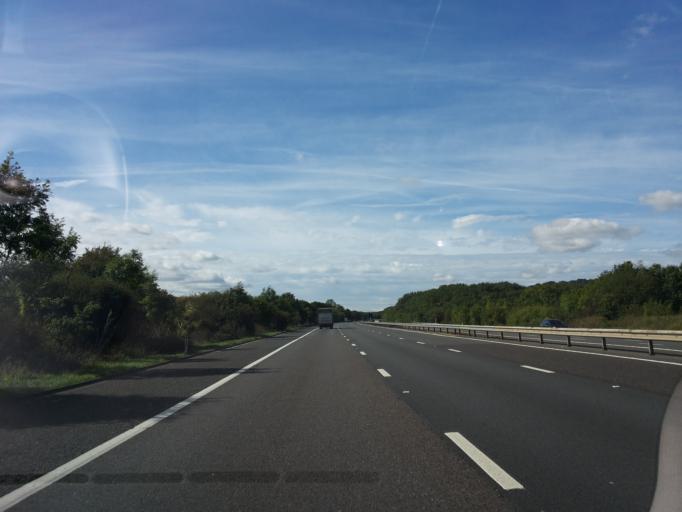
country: GB
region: England
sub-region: Kent
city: Borough Green
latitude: 51.3067
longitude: 0.3437
